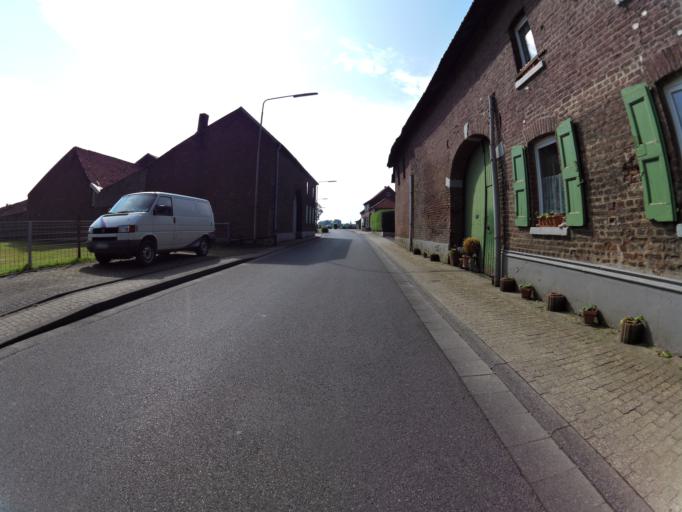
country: DE
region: North Rhine-Westphalia
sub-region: Regierungsbezirk Koln
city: Waldfeucht
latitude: 51.0733
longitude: 5.9978
